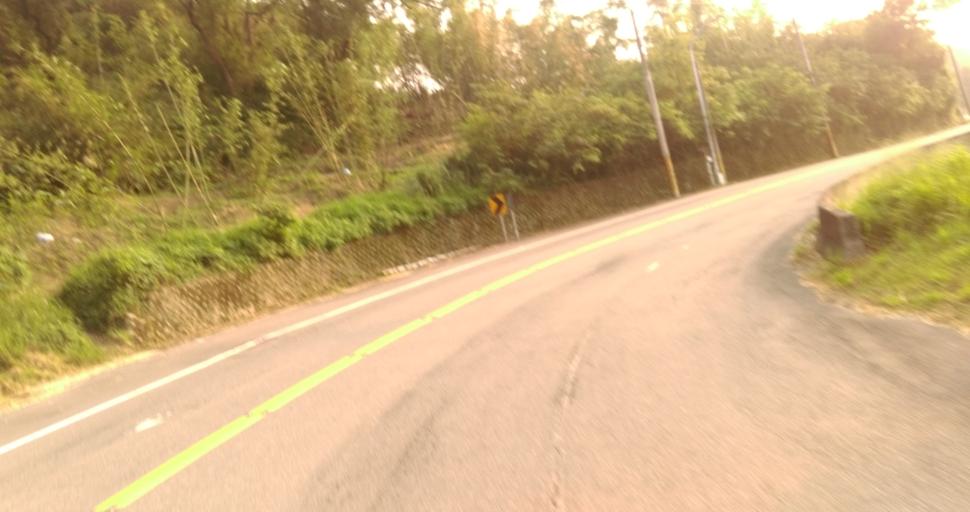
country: TW
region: Taiwan
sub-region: Hsinchu
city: Hsinchu
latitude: 24.7571
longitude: 120.9434
